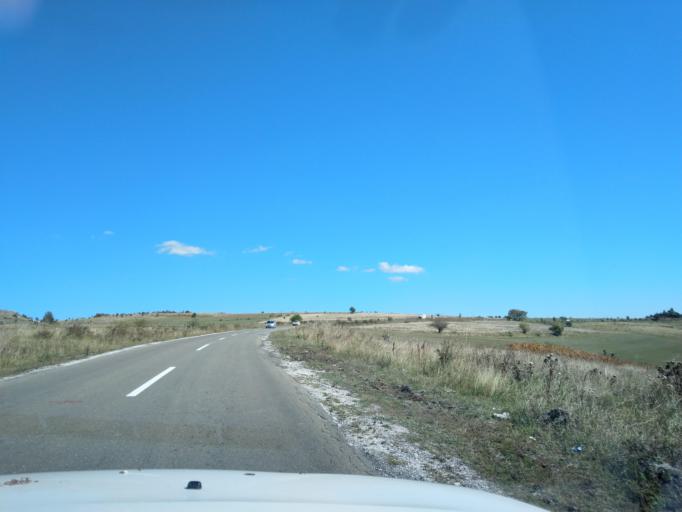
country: RS
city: Sokolovica
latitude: 43.2767
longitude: 20.2151
